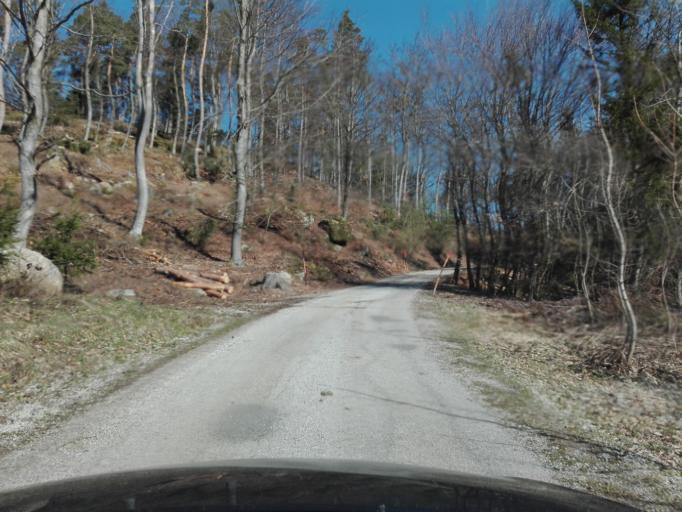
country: AT
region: Upper Austria
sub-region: Politischer Bezirk Perg
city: Bad Kreuzen
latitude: 48.3739
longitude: 14.7636
